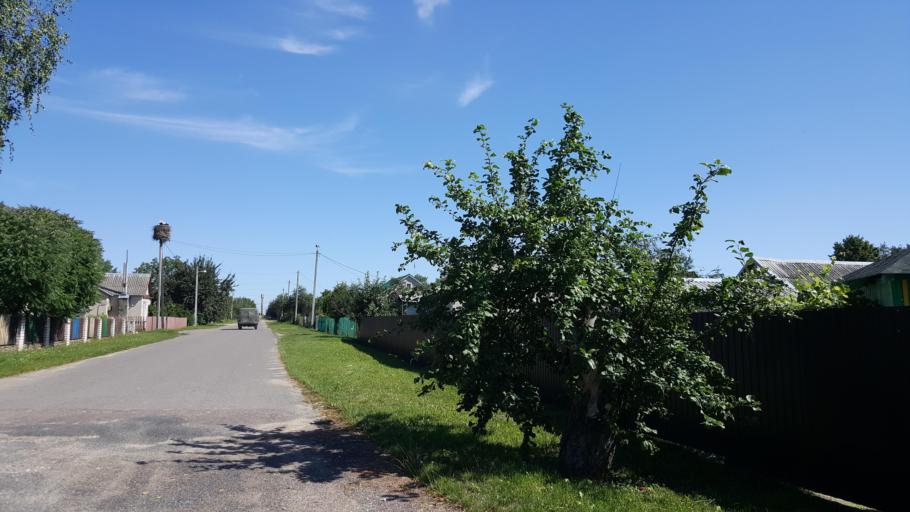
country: BY
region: Brest
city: Charnawchytsy
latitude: 52.2735
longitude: 23.7657
